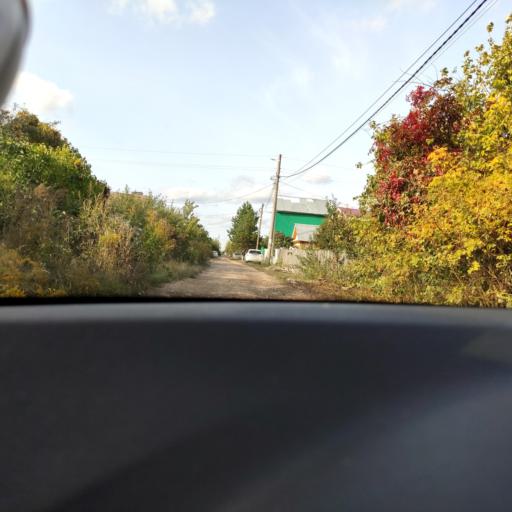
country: RU
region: Samara
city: Petra-Dubrava
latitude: 53.2825
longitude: 50.2954
